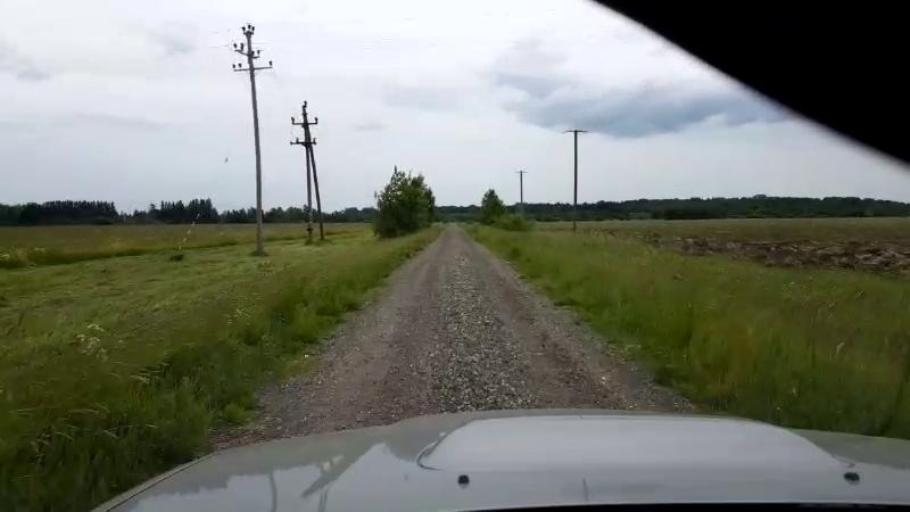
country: EE
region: Paernumaa
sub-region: Halinga vald
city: Parnu-Jaagupi
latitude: 58.5306
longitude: 24.6119
